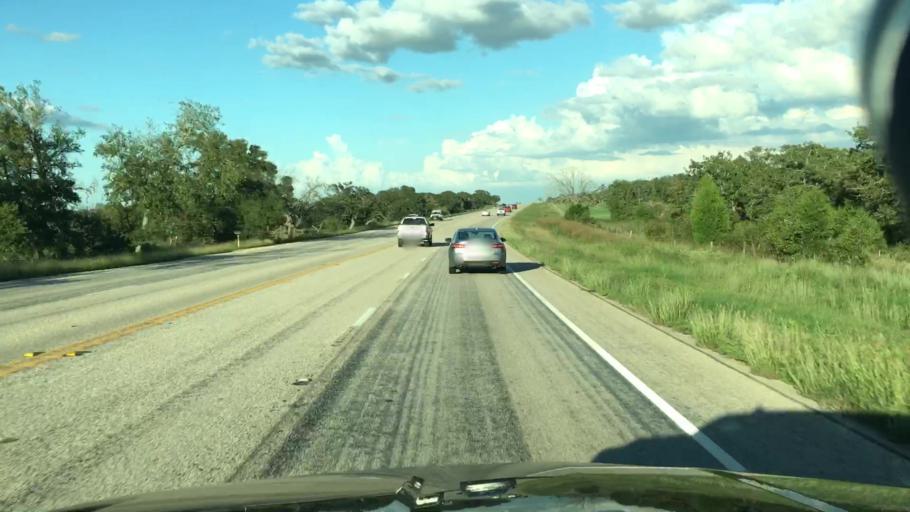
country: US
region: Texas
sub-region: Lee County
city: Lexington
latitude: 30.3155
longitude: -96.9389
